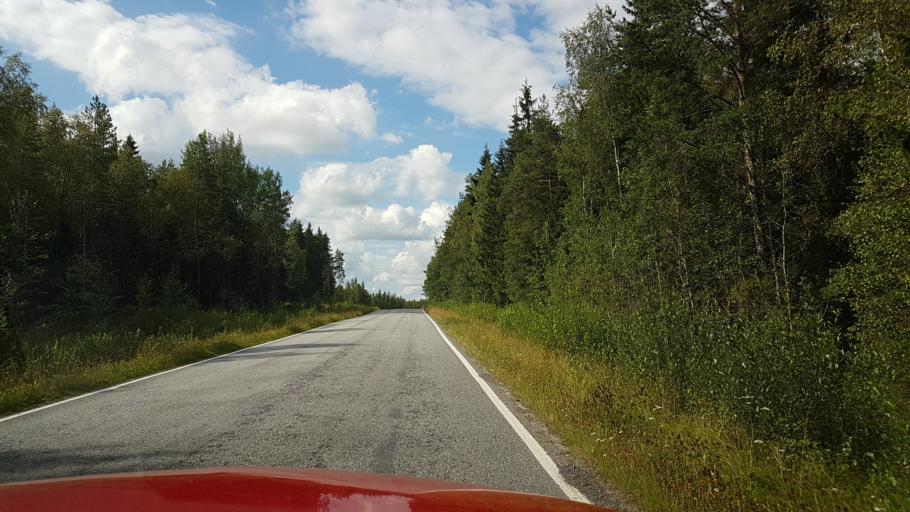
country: FI
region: Northern Ostrobothnia
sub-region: Ylivieska
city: Himanka
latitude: 64.0739
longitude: 23.7012
